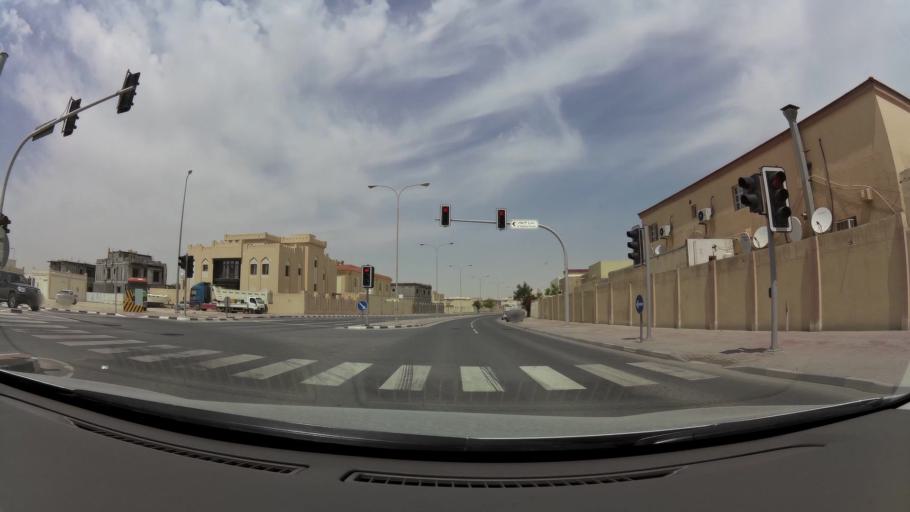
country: QA
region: Baladiyat ar Rayyan
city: Ar Rayyan
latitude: 25.2942
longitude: 51.4125
